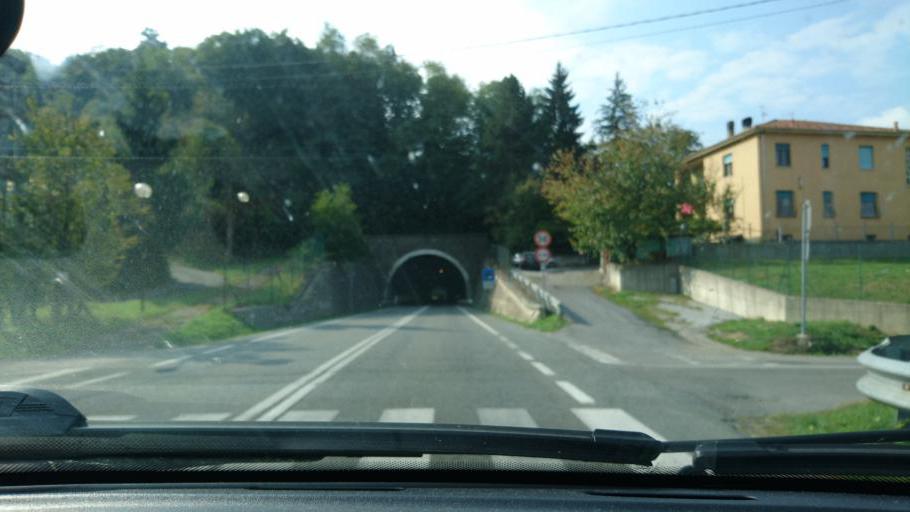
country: IT
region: Liguria
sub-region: Provincia di Savona
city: Dego
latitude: 44.4272
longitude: 8.3021
